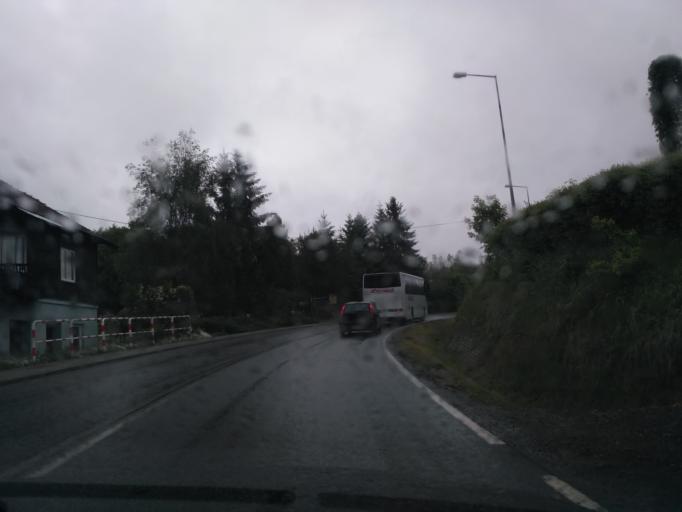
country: PL
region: Lesser Poland Voivodeship
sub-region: Powiat gorlicki
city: Gorlice
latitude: 49.6716
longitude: 21.1414
